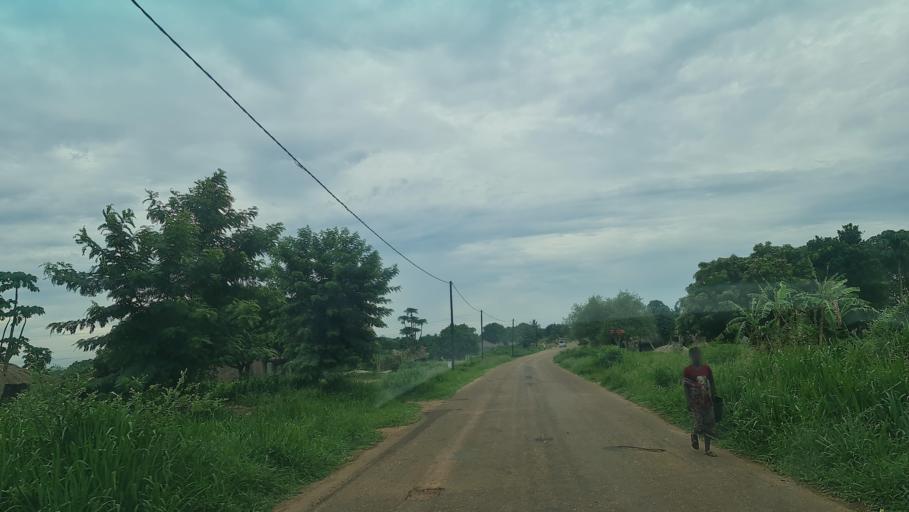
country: MW
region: Southern Region
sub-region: Nsanje District
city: Nsanje
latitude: -17.6735
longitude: 35.7177
